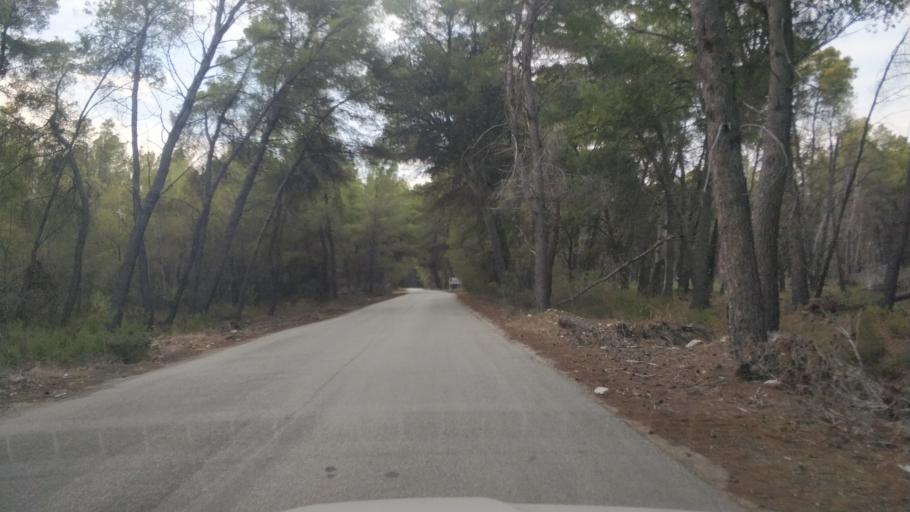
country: AL
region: Vlore
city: Vlore
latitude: 40.4838
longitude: 19.4469
